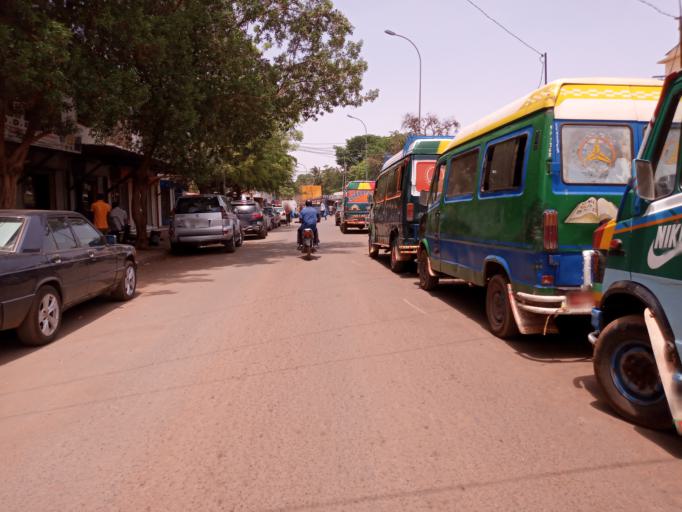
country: ML
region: Bamako
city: Bamako
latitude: 12.6426
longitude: -8.0016
